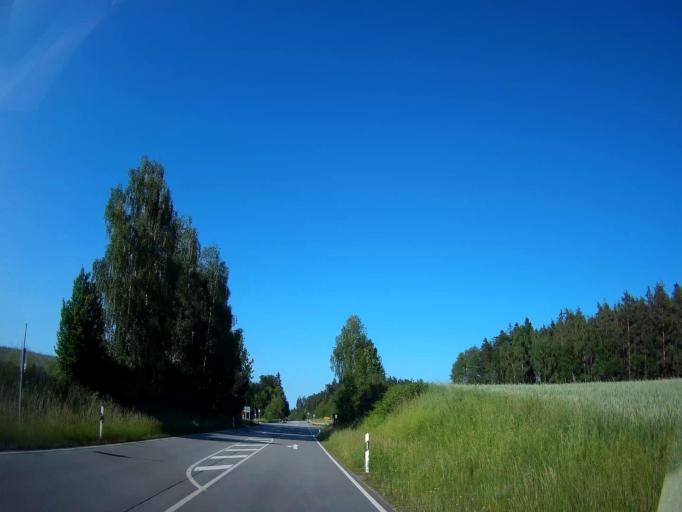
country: DE
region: Bavaria
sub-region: Lower Bavaria
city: Malgersdorf
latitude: 48.5172
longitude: 12.7434
